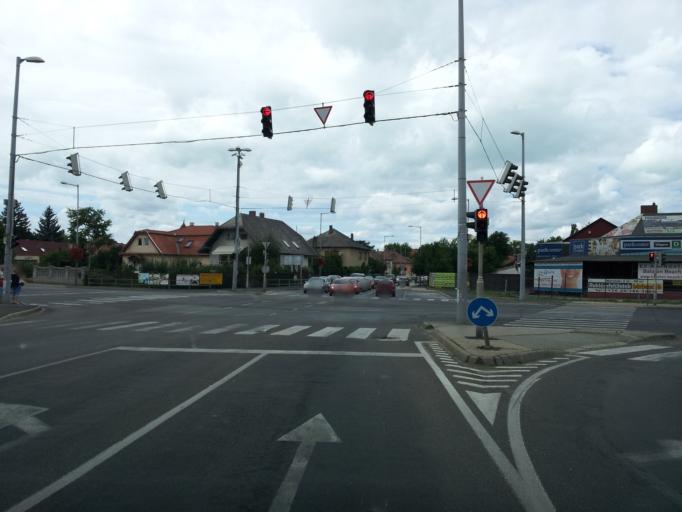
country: HU
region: Somogy
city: Siofok
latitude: 46.9023
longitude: 18.0480
